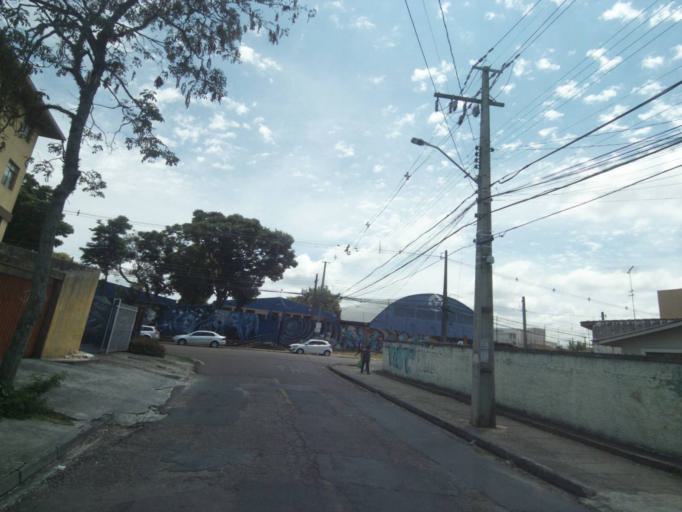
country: BR
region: Parana
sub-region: Curitiba
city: Curitiba
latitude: -25.4578
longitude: -49.3486
